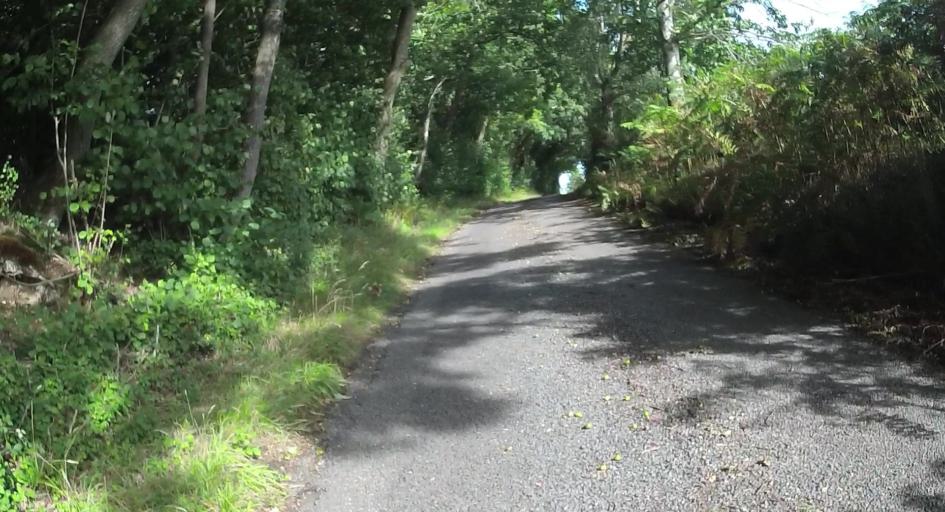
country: GB
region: England
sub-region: Hampshire
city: Kingsclere
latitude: 51.3645
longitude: -1.1988
